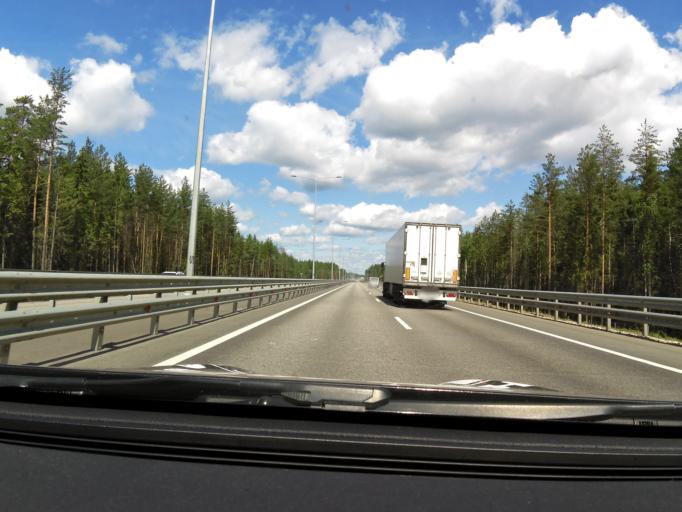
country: RU
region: Tverskaya
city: Krasnomayskiy
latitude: 57.5719
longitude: 34.2605
